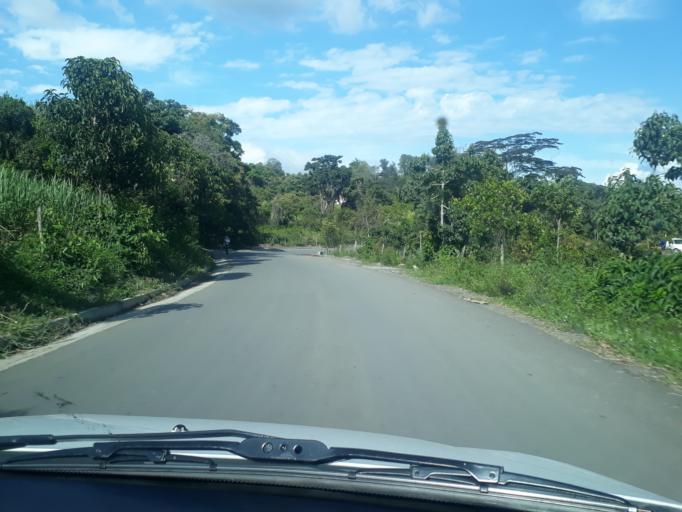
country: CO
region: Santander
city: Velez
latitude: 6.0585
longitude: -73.6430
